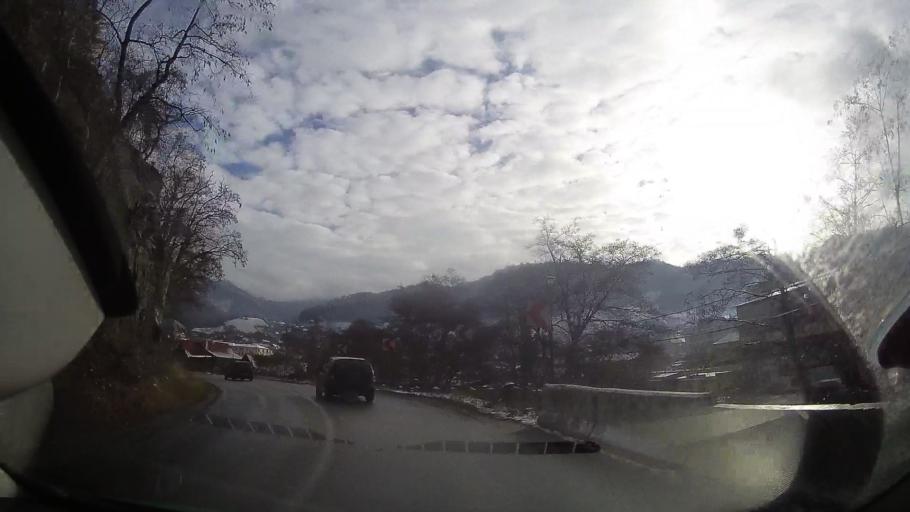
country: RO
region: Alba
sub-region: Oras Baia de Aries
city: Baia de Aries
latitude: 46.3818
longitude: 23.2794
